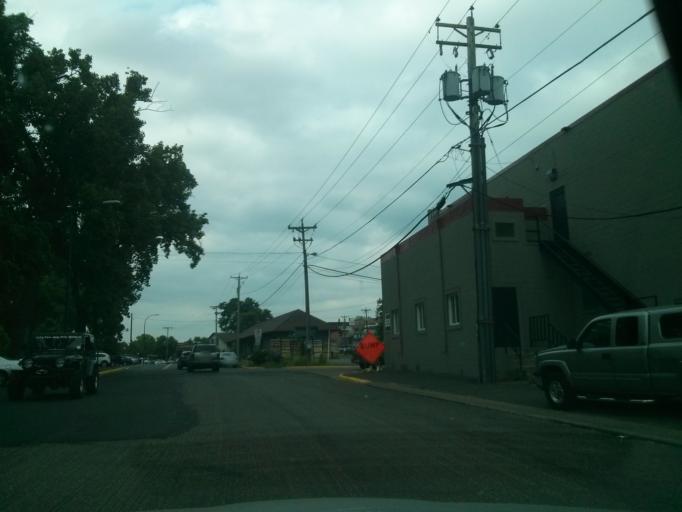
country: US
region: Wisconsin
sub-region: Saint Croix County
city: Hudson
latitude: 44.9724
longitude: -92.7579
